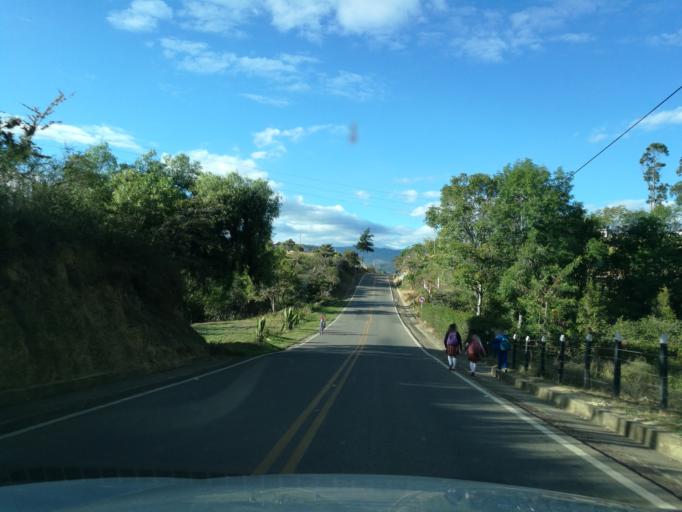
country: CO
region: Boyaca
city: Sutamarchan
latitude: 5.5984
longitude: -73.6383
